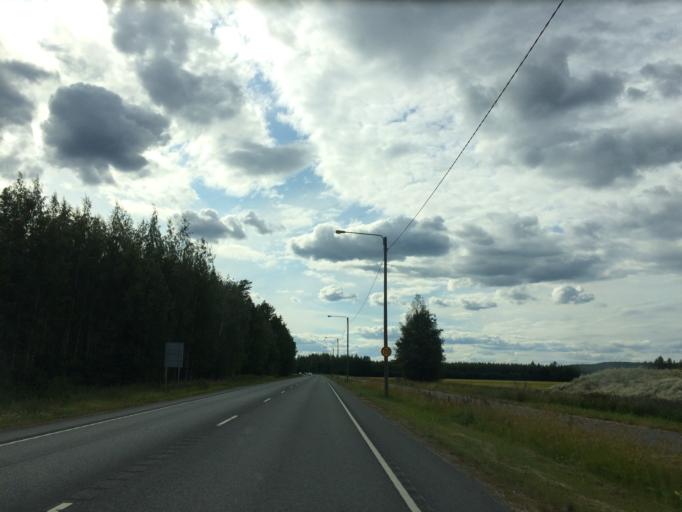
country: FI
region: Haeme
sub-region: Haemeenlinna
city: Janakkala
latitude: 60.9215
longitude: 24.6055
